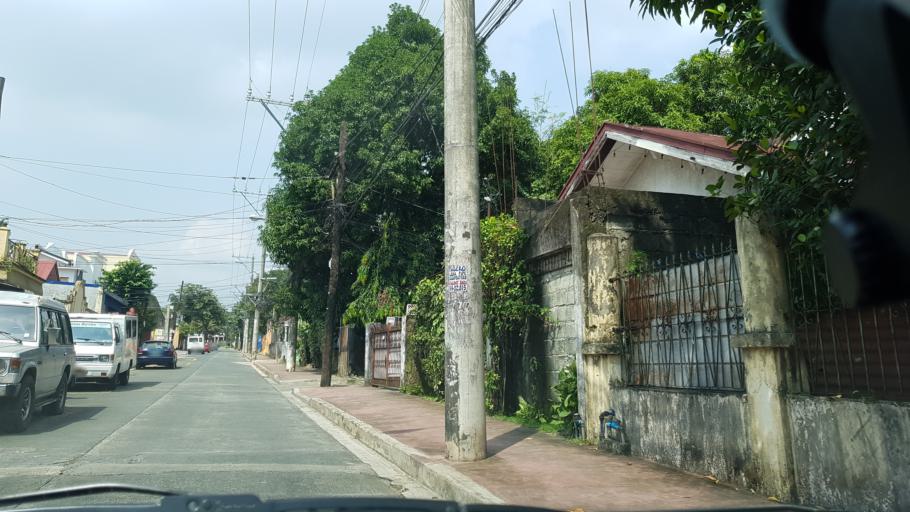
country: PH
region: Calabarzon
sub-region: Province of Rizal
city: Antipolo
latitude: 14.6497
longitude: 121.1194
